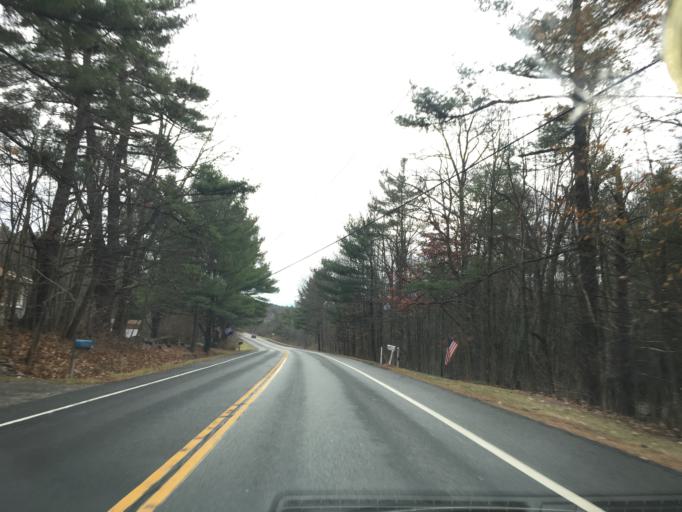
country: US
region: New York
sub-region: Rensselaer County
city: Averill Park
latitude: 42.6433
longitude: -73.5478
